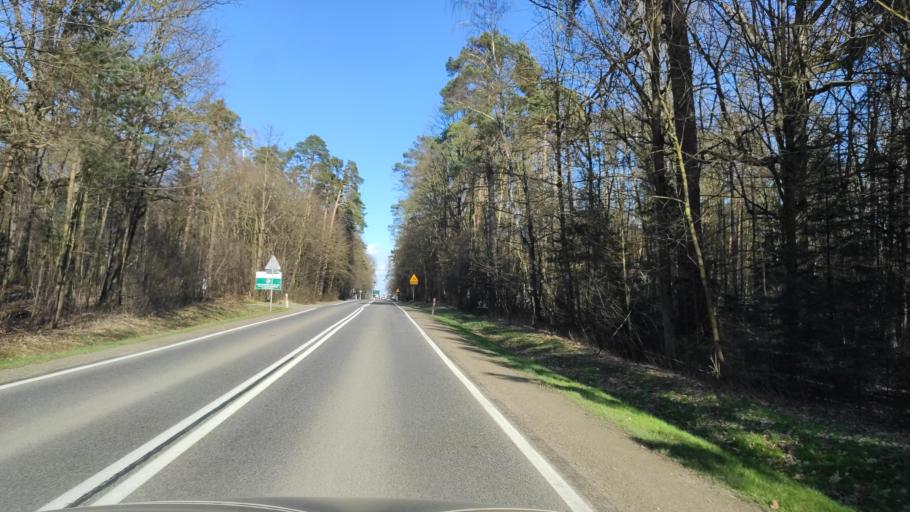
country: PL
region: Masovian Voivodeship
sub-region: Powiat radomski
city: Jedlnia-Letnisko
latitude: 51.4456
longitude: 21.3227
